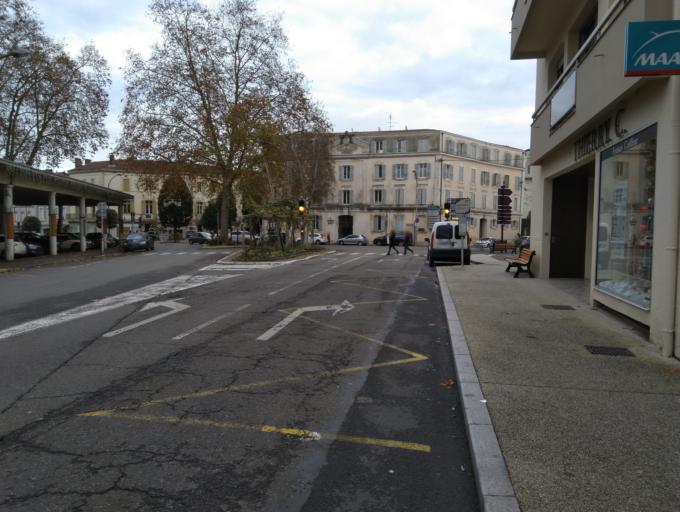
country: FR
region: Aquitaine
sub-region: Departement des Landes
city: Dax
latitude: 43.7083
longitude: -1.0557
